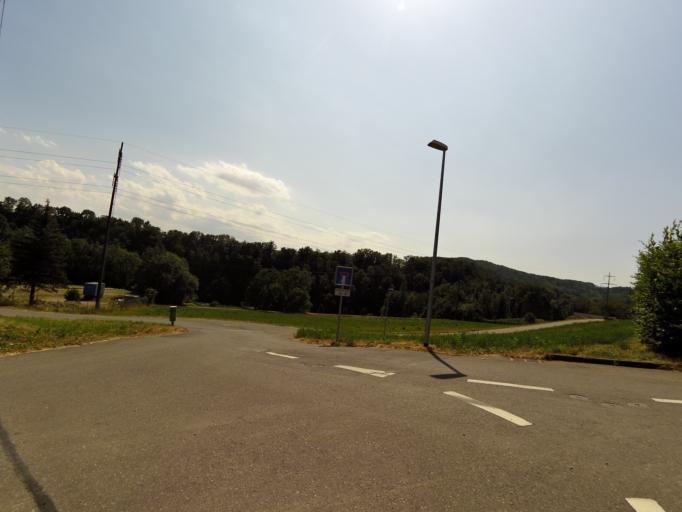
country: CH
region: Aargau
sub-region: Bezirk Baden
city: Birmenstorf
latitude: 47.4587
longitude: 8.2502
